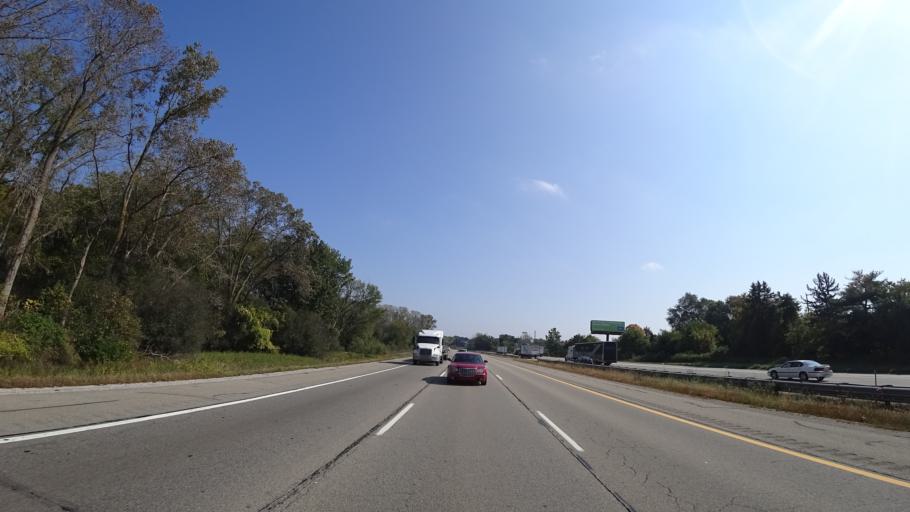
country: US
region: Michigan
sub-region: Washtenaw County
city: Dexter
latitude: 42.2893
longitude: -83.8311
